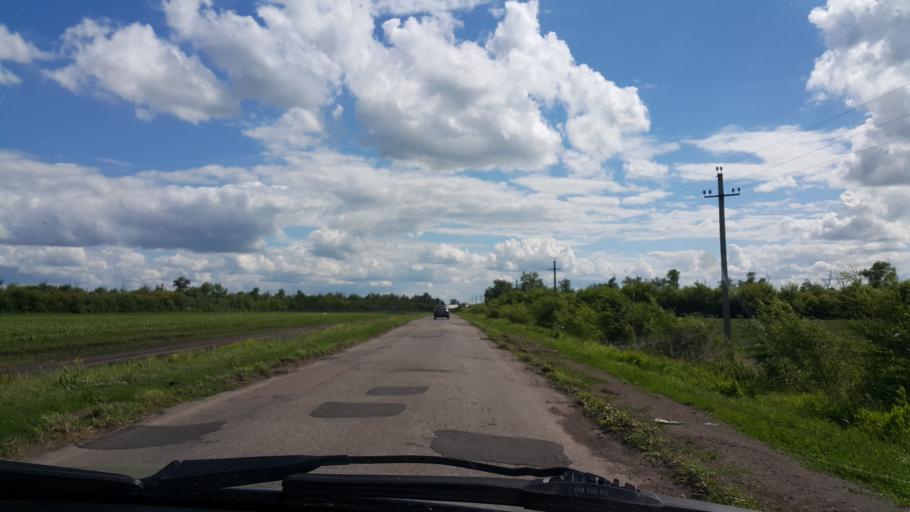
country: RU
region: Tambov
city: Satinka
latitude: 52.3923
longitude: 41.6639
